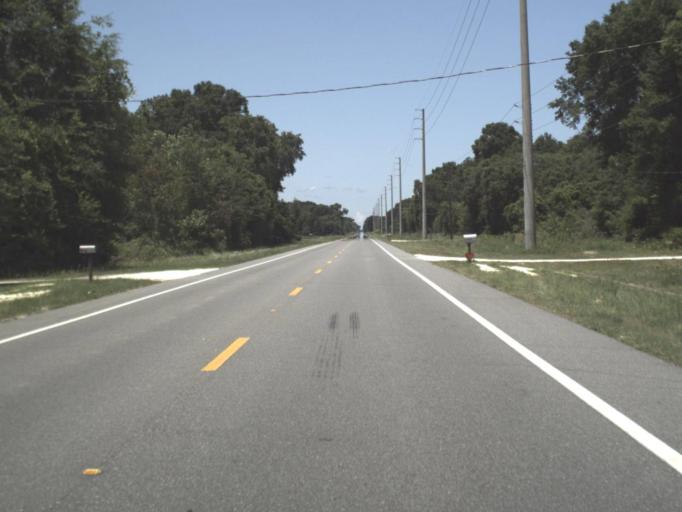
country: US
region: Florida
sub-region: Dixie County
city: Cross City
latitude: 29.6919
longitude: -82.9843
